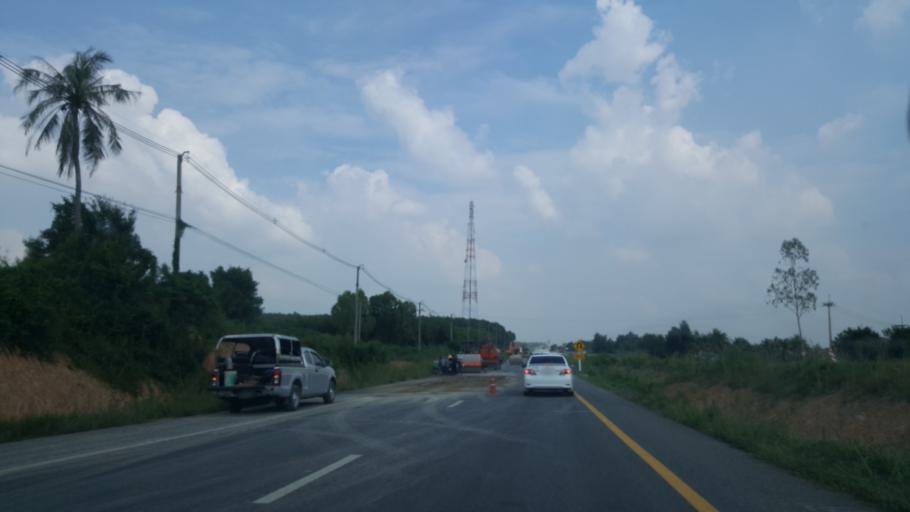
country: TH
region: Rayong
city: Ban Chang
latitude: 12.8682
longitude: 101.0239
